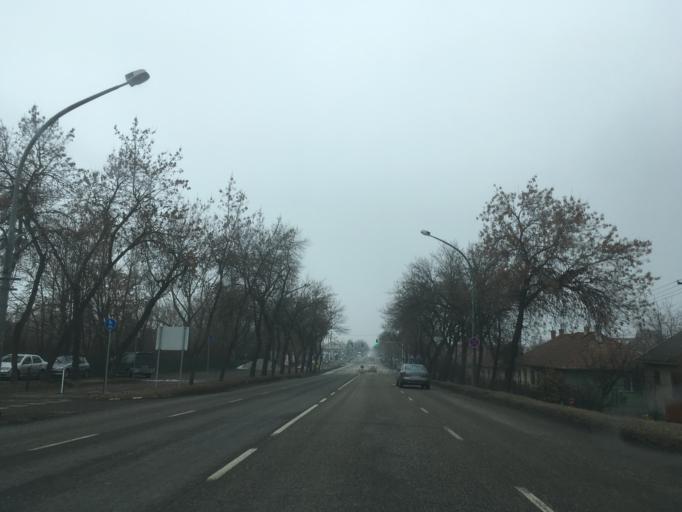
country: HU
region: Heves
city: Eger
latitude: 47.8732
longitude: 20.3828
